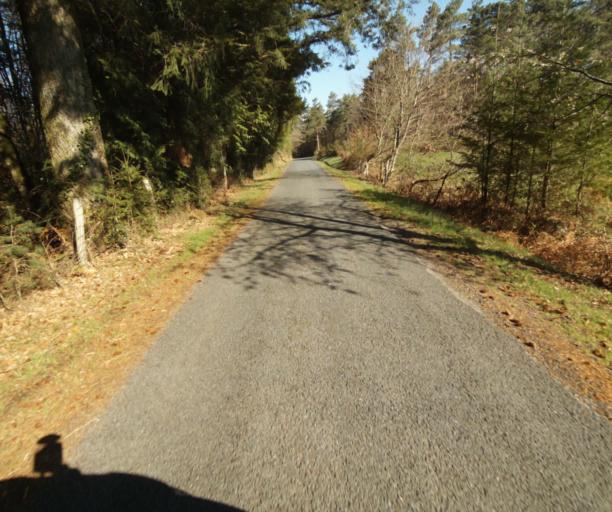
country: FR
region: Limousin
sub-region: Departement de la Correze
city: Correze
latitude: 45.2757
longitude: 1.9233
